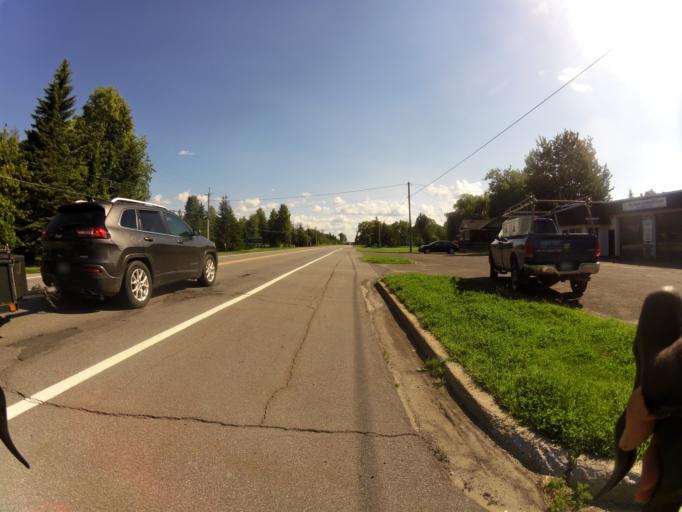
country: CA
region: Ontario
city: Ottawa
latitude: 45.3179
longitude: -75.6917
